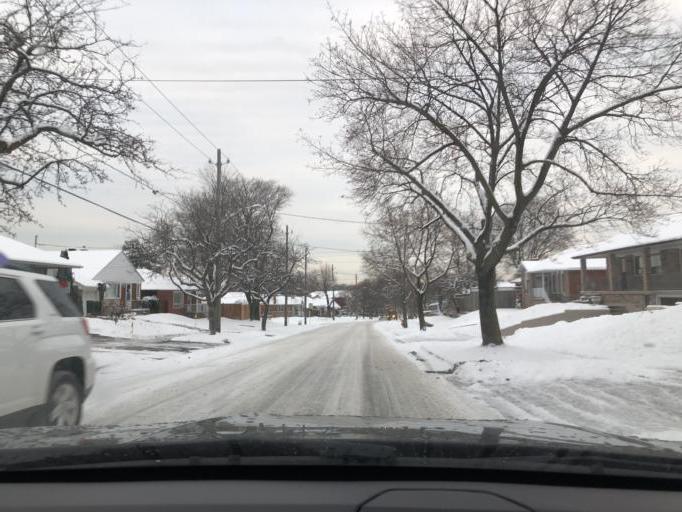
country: CA
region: Ontario
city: Toronto
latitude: 43.7045
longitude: -79.4807
